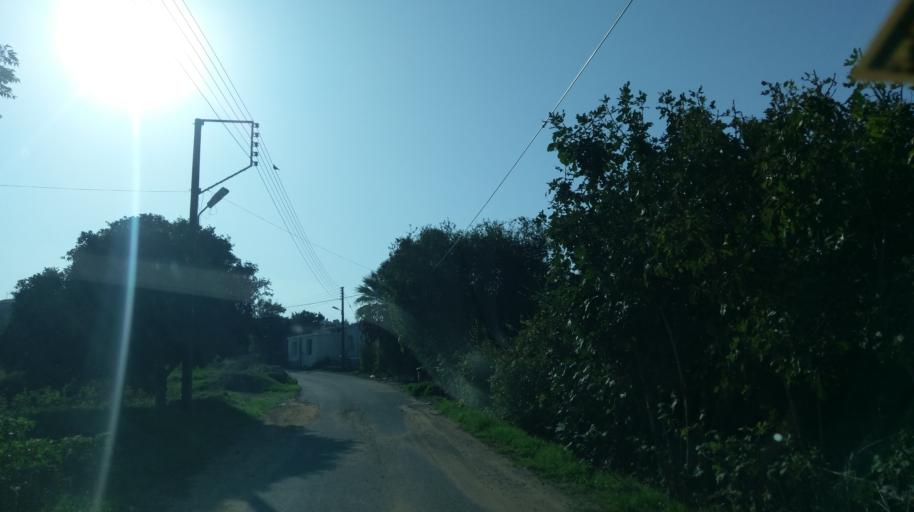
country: CY
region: Ammochostos
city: Leonarisso
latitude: 35.5395
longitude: 34.1919
